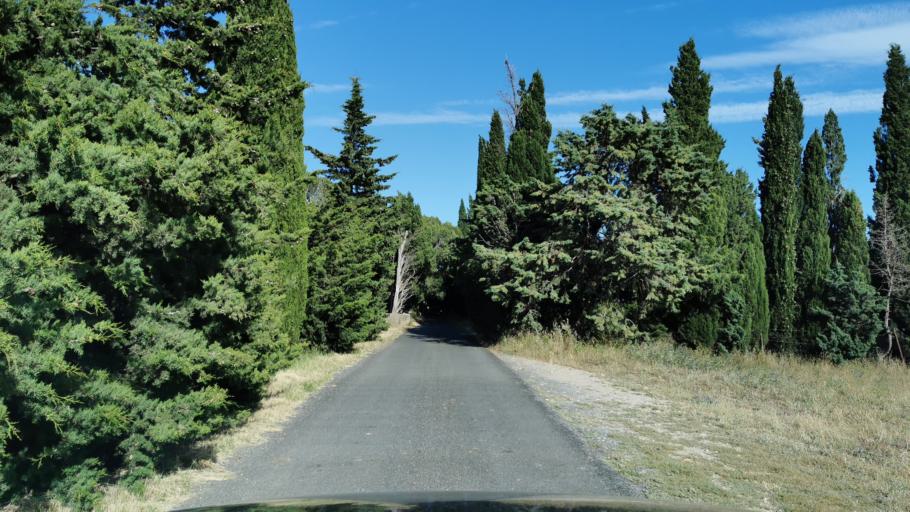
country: FR
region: Languedoc-Roussillon
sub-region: Departement de l'Aude
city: Narbonne
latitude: 43.1567
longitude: 3.0087
